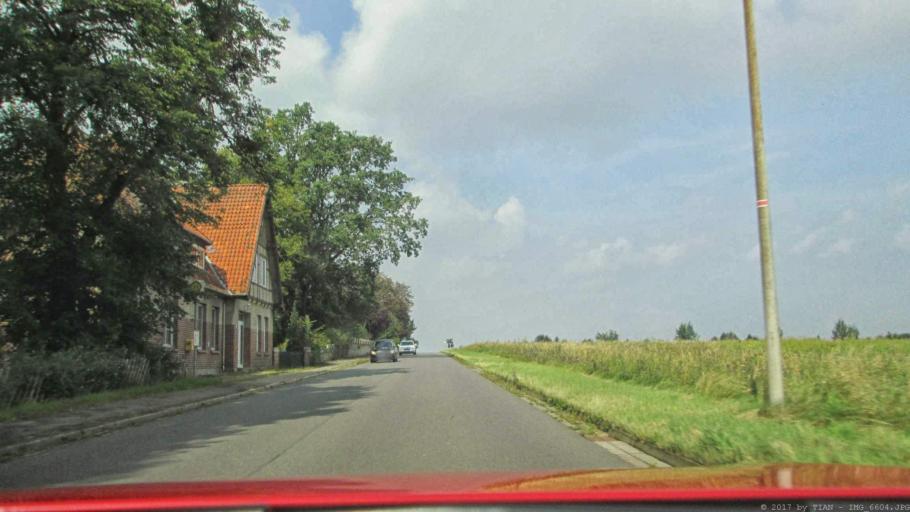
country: DE
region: Lower Saxony
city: Uelzen
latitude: 52.9401
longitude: 10.5775
